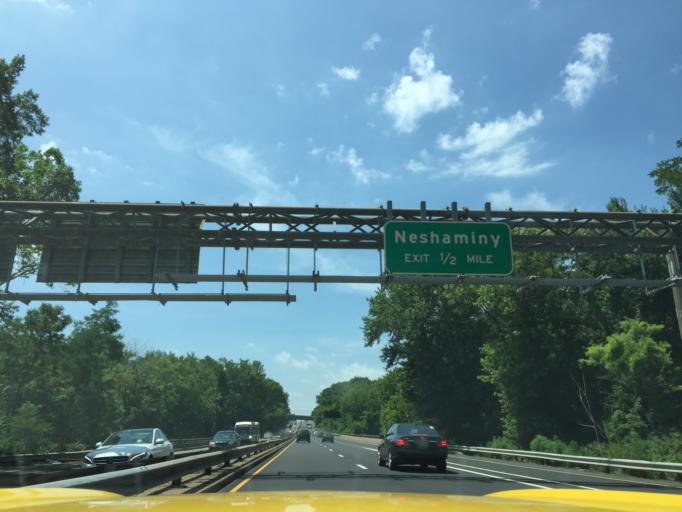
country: US
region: Pennsylvania
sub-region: Bucks County
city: Trevose
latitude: 40.1464
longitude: -74.9532
